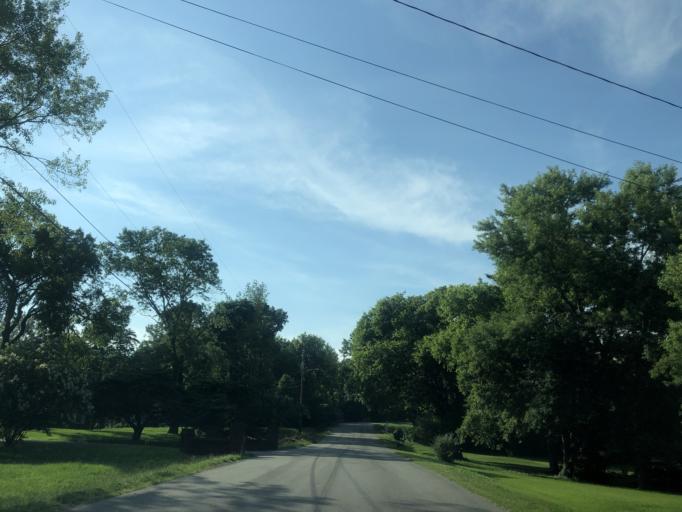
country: US
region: Tennessee
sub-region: Davidson County
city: Nashville
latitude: 36.2420
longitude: -86.8356
